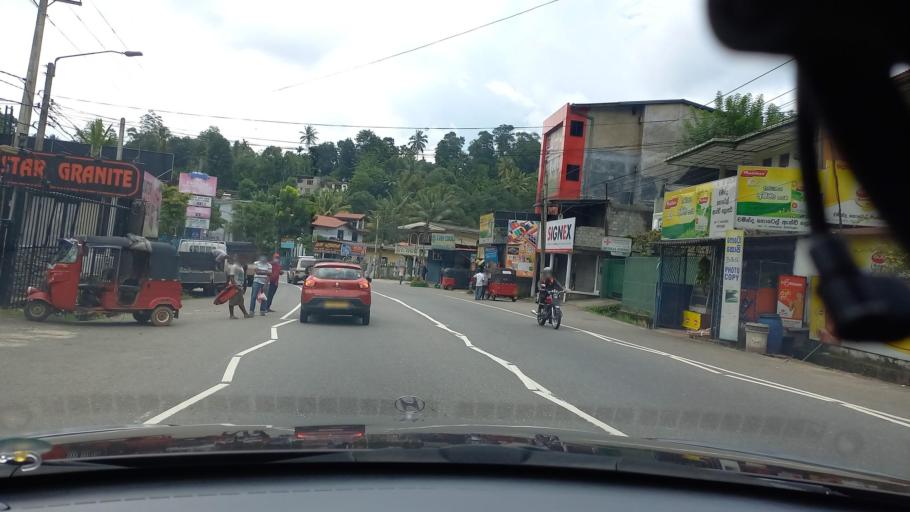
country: LK
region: Central
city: Kadugannawa
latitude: 7.2682
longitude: 80.5809
